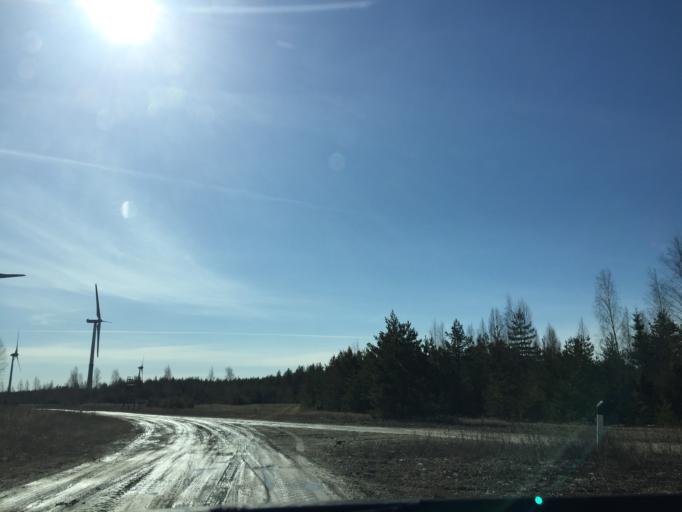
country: EE
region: Laeaene
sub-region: Haapsalu linn
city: Haapsalu
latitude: 58.6319
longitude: 23.5254
